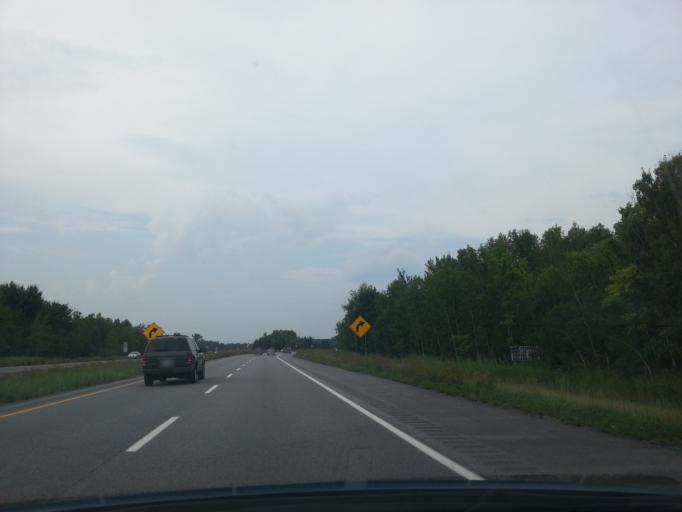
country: CA
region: Quebec
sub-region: Monteregie
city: Rigaud
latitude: 45.5259
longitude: -74.3782
